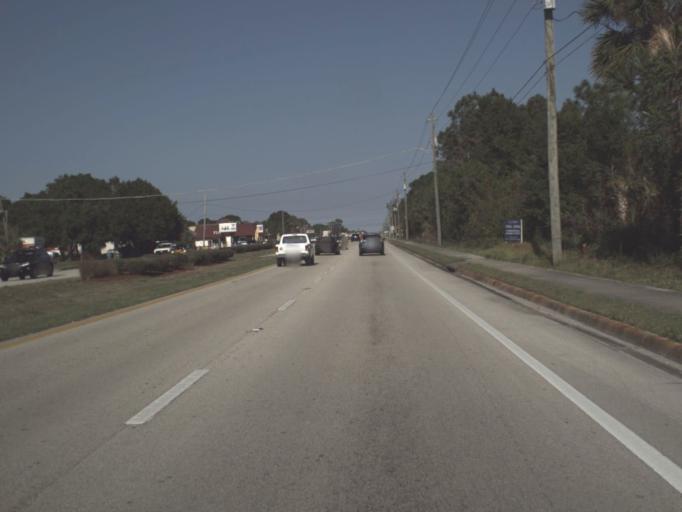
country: US
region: Florida
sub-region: Brevard County
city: June Park
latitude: 28.0788
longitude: -80.6895
